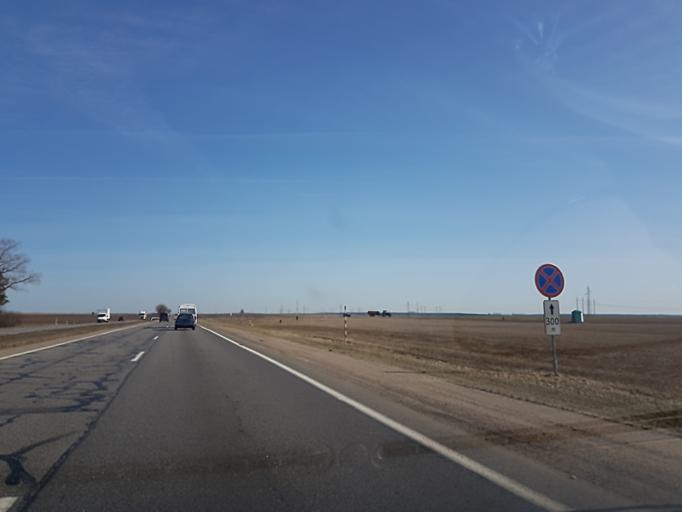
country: BY
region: Minsk
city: Dukora
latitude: 53.6948
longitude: 27.8956
